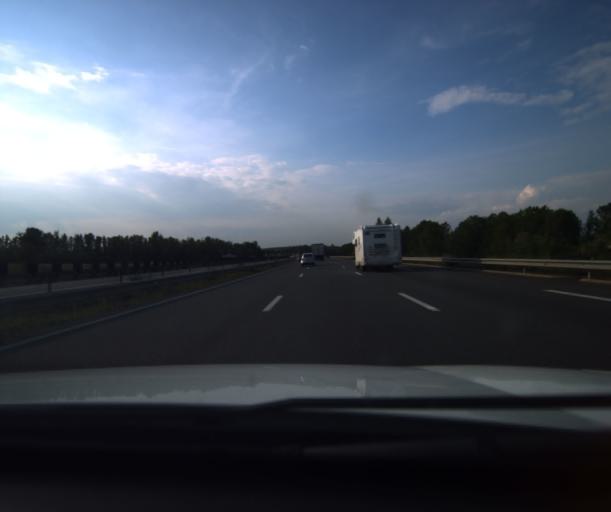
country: FR
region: Midi-Pyrenees
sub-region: Departement du Tarn-et-Garonne
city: Campsas
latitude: 43.9179
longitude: 1.3183
